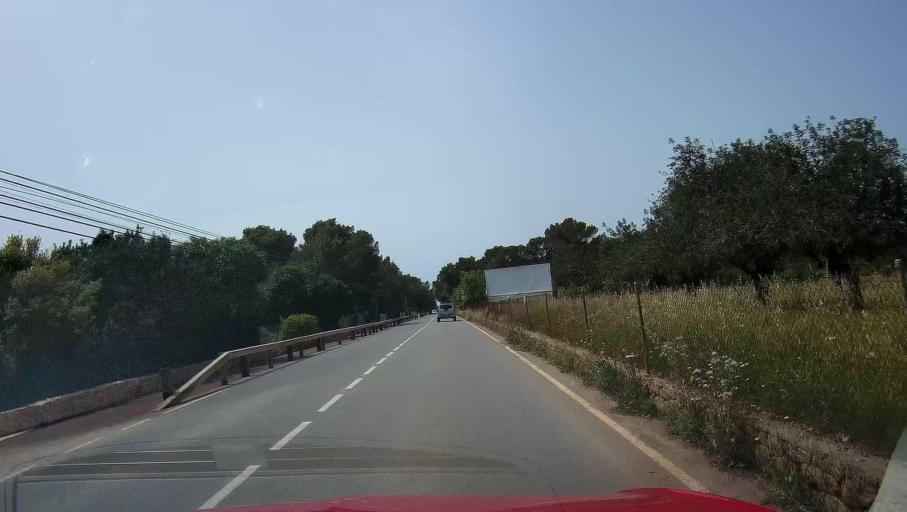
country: ES
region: Balearic Islands
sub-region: Illes Balears
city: Santa Eularia des Riu
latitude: 39.0013
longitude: 1.5646
